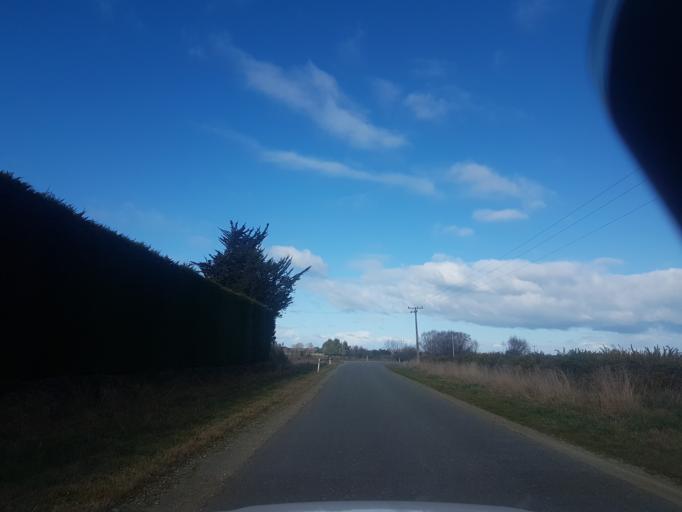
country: NZ
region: Canterbury
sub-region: Timaru District
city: Pleasant Point
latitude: -44.2253
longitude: 171.2346
